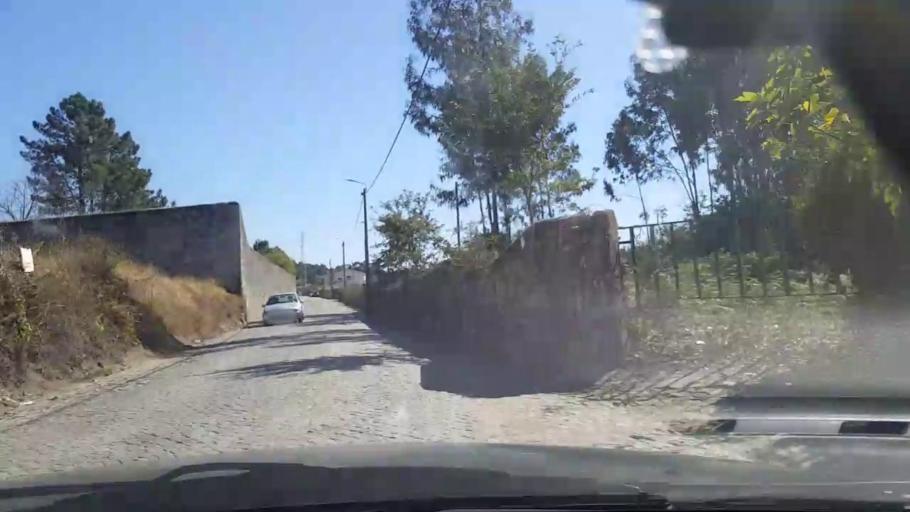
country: PT
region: Porto
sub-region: Vila do Conde
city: Arvore
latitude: 41.3201
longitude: -8.6992
